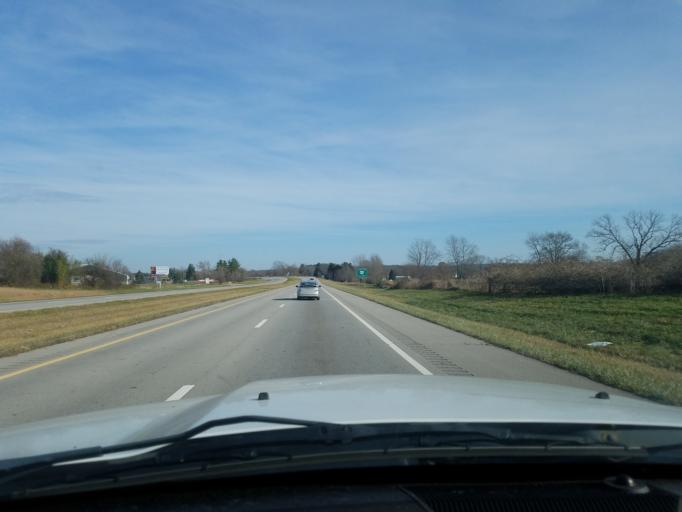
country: US
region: Ohio
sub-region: Athens County
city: Athens
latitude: 39.2222
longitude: -82.2065
